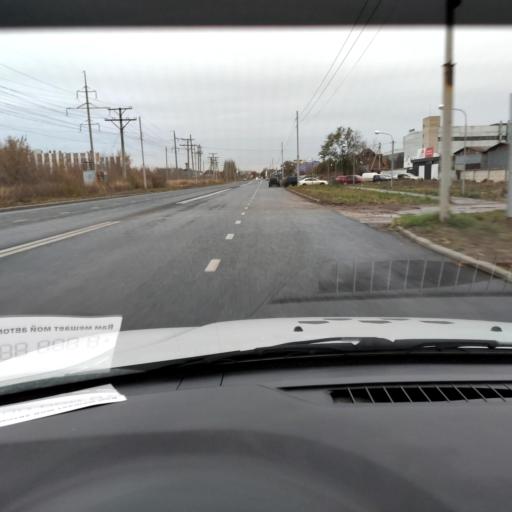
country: RU
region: Samara
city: Tol'yatti
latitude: 53.5547
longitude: 49.2935
